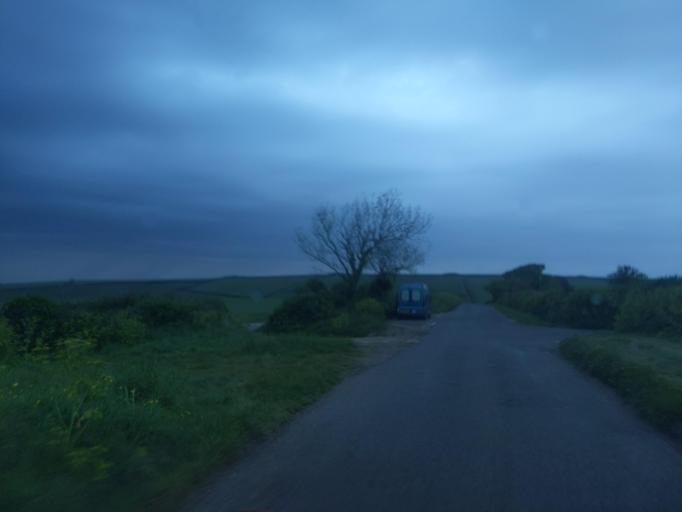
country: GB
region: England
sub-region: Devon
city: Dartmouth
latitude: 50.3613
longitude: -3.5485
